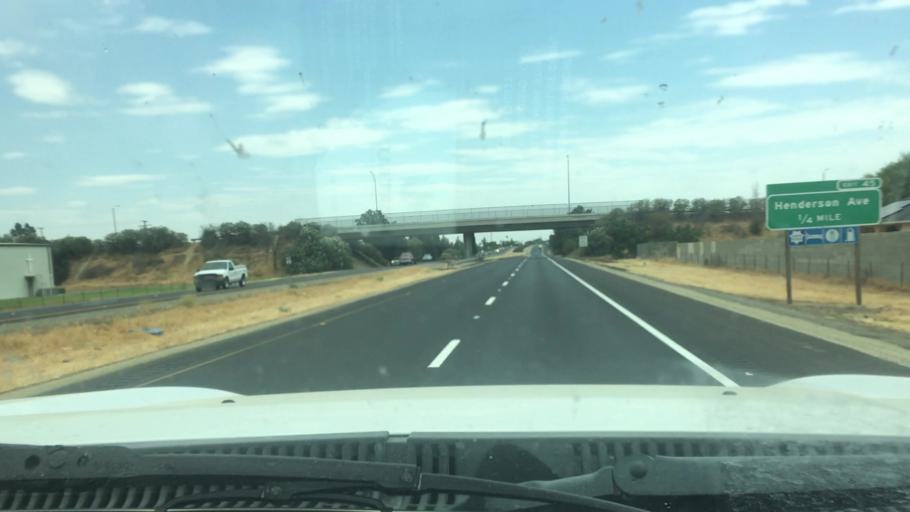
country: US
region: California
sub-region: Tulare County
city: Porterville
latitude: 36.0891
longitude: -119.0396
